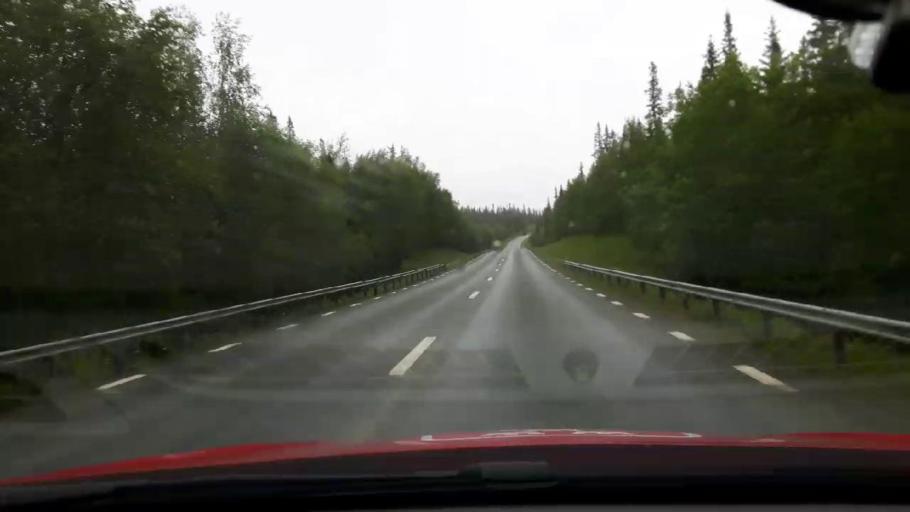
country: NO
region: Nord-Trondelag
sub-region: Meraker
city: Meraker
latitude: 63.2710
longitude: 12.2684
